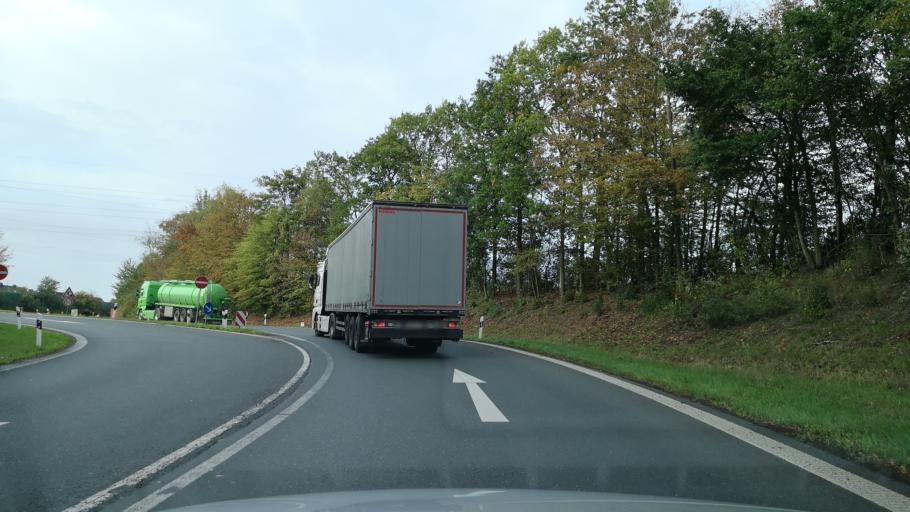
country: DE
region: North Rhine-Westphalia
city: Herdecke
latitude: 51.4048
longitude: 7.4699
